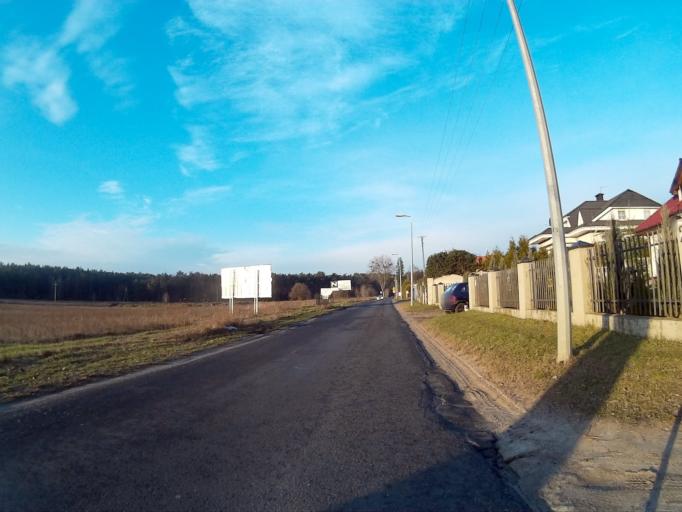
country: PL
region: Kujawsko-Pomorskie
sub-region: Powiat bydgoski
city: Osielsko
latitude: 53.1602
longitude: 18.0752
